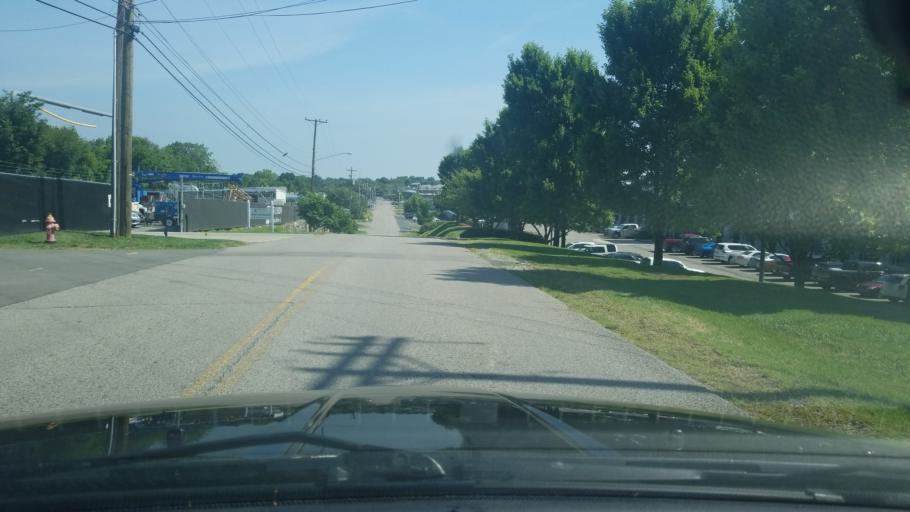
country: US
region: Tennessee
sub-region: Davidson County
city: Oak Hill
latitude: 36.1057
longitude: -86.7586
